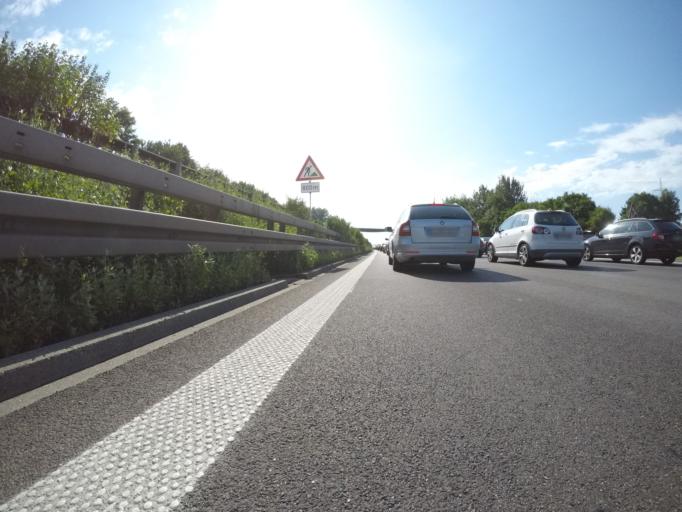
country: DE
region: Baden-Wuerttemberg
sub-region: Regierungsbezirk Stuttgart
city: Kirchheim unter Teck
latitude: 48.6333
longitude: 9.4469
